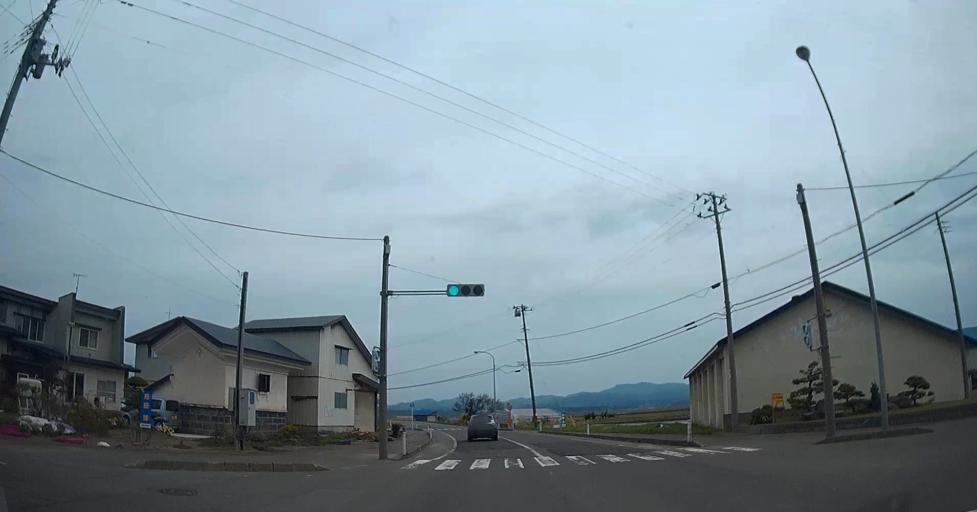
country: JP
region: Aomori
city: Shimokizukuri
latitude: 40.9782
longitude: 140.3740
